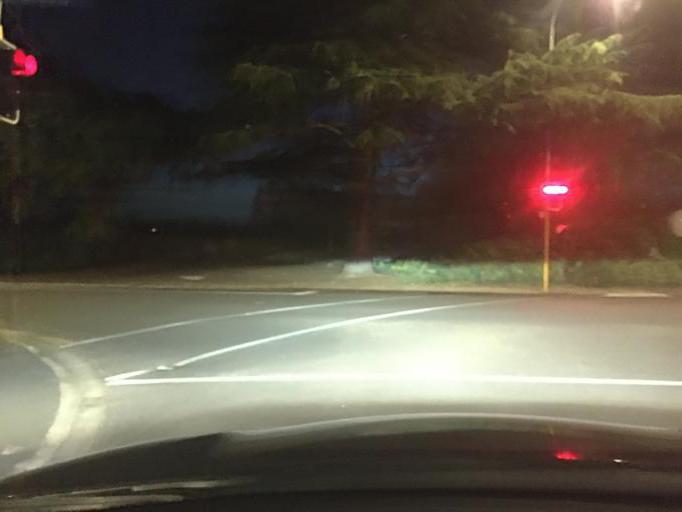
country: NZ
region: Waikato
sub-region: Hamilton City
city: Hamilton
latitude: -37.7857
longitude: 175.2750
